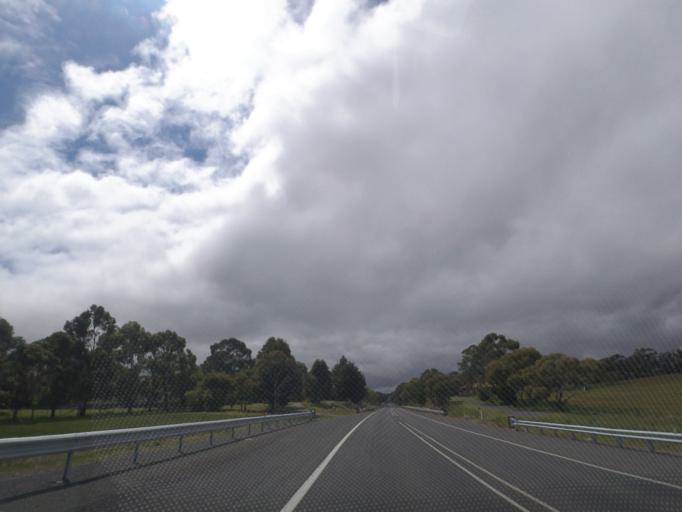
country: AU
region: Victoria
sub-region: Ballarat North
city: Soldiers Hill
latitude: -37.4628
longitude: 143.8528
